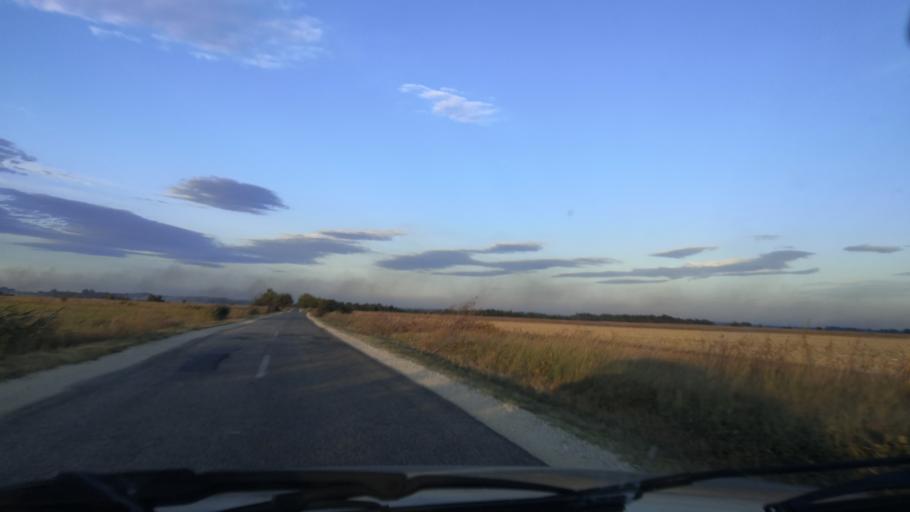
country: RS
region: Central Serbia
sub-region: Borski Okrug
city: Negotin
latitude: 44.2450
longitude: 22.5746
